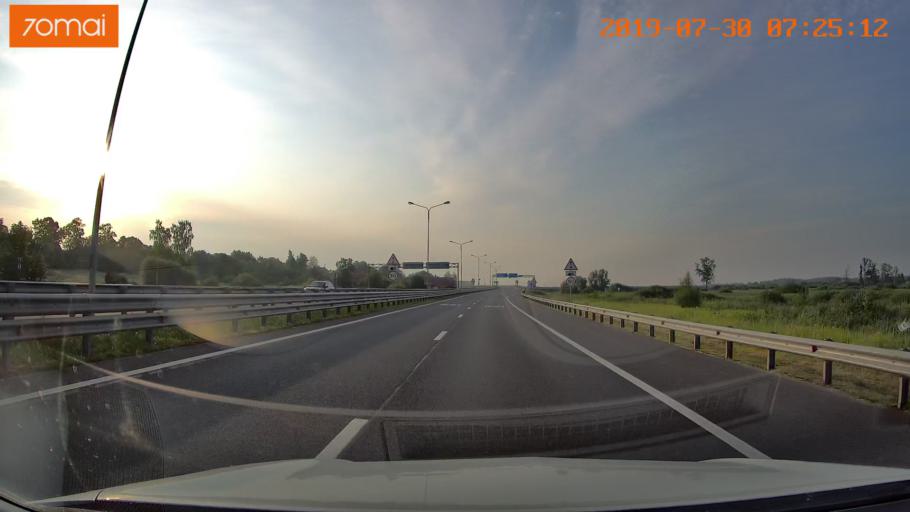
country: RU
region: Kaliningrad
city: Bol'shoe Isakovo
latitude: 54.6883
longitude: 20.8309
